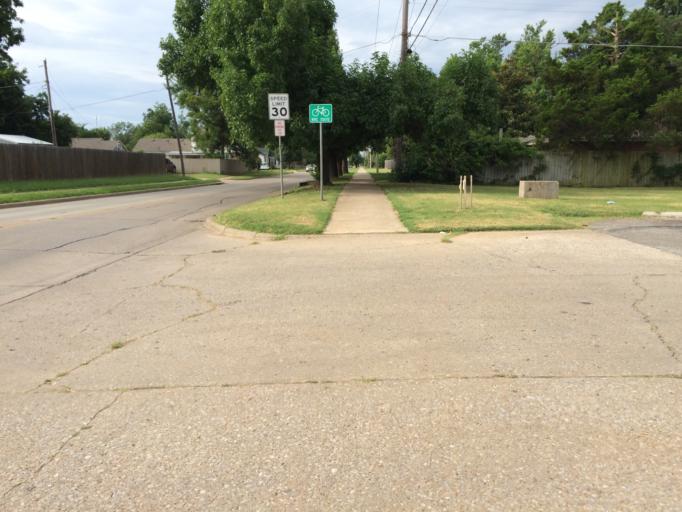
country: US
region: Oklahoma
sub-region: Cleveland County
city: Norman
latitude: 35.2242
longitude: -97.4591
